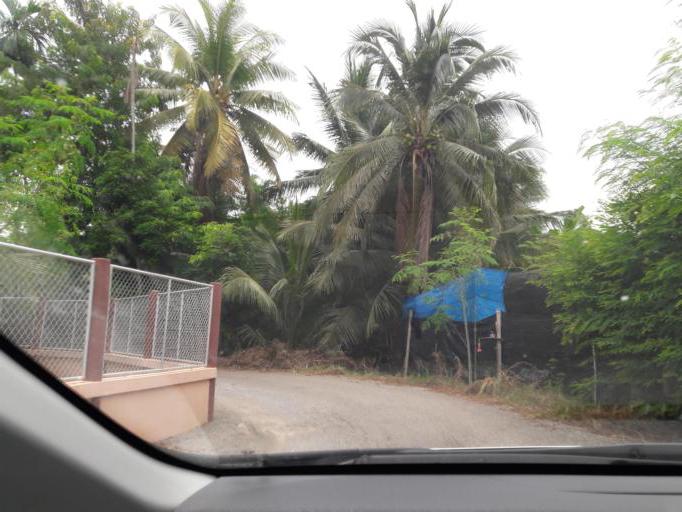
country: TH
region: Samut Sakhon
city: Ban Phaeo
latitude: 13.5912
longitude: 100.0274
